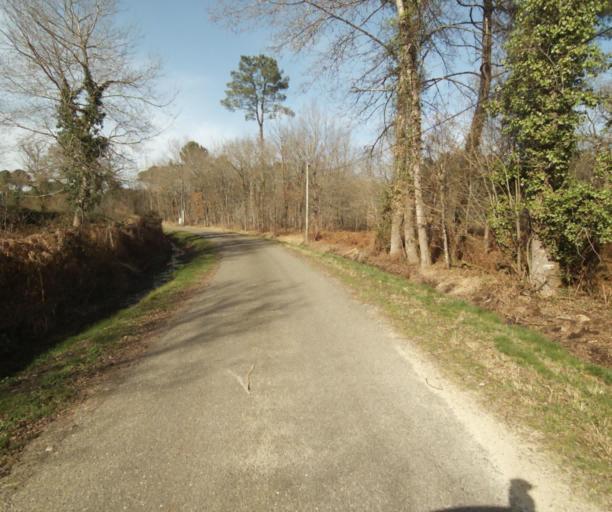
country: FR
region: Aquitaine
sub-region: Departement des Landes
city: Roquefort
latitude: 44.1558
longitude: -0.1960
